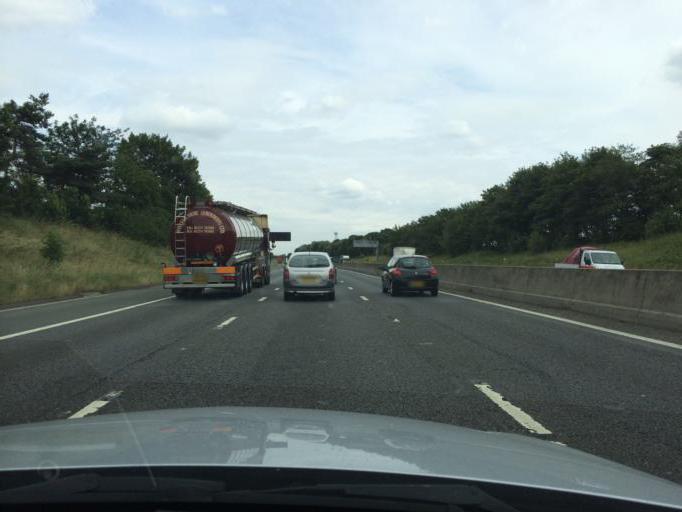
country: GB
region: England
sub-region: City and Borough of Salford
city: Irlam
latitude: 53.4433
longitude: -2.4470
